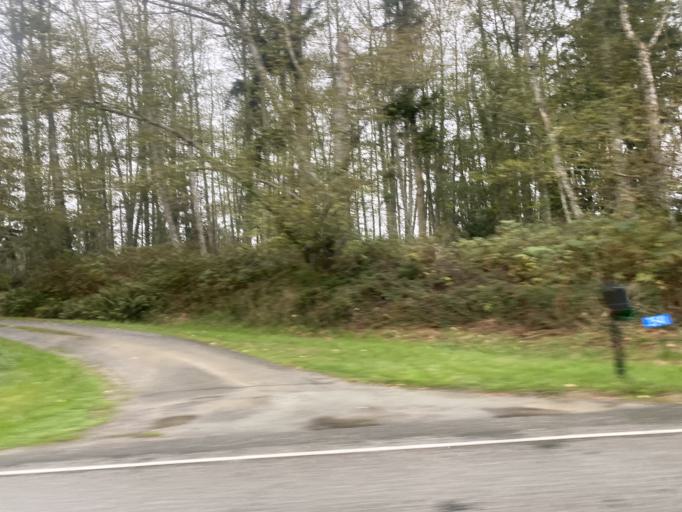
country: US
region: Washington
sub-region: Island County
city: Freeland
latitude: 48.0825
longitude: -122.4931
